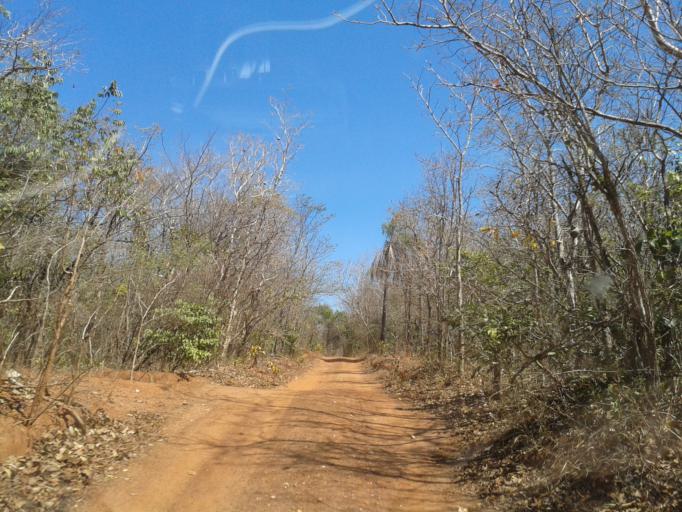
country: BR
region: Minas Gerais
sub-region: Ituiutaba
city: Ituiutaba
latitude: -19.1241
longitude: -49.3001
